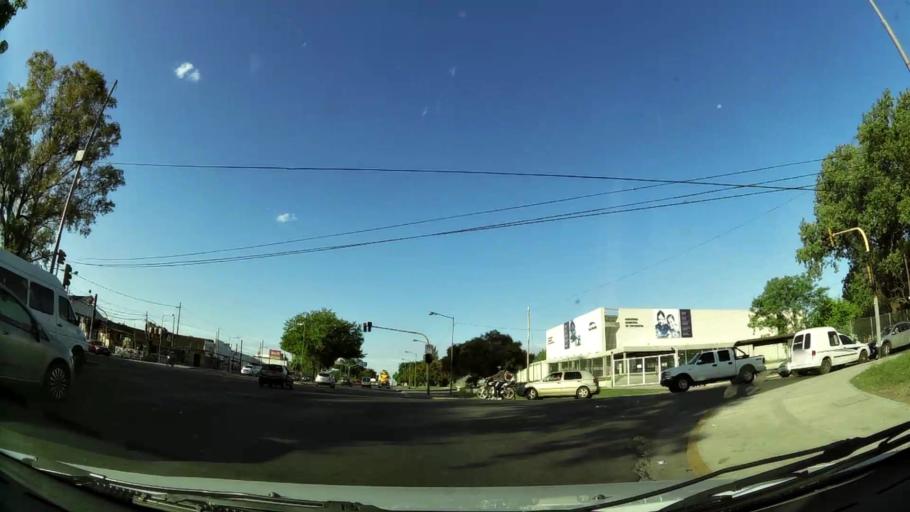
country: AR
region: Buenos Aires
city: Caseros
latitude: -34.5481
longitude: -58.5825
